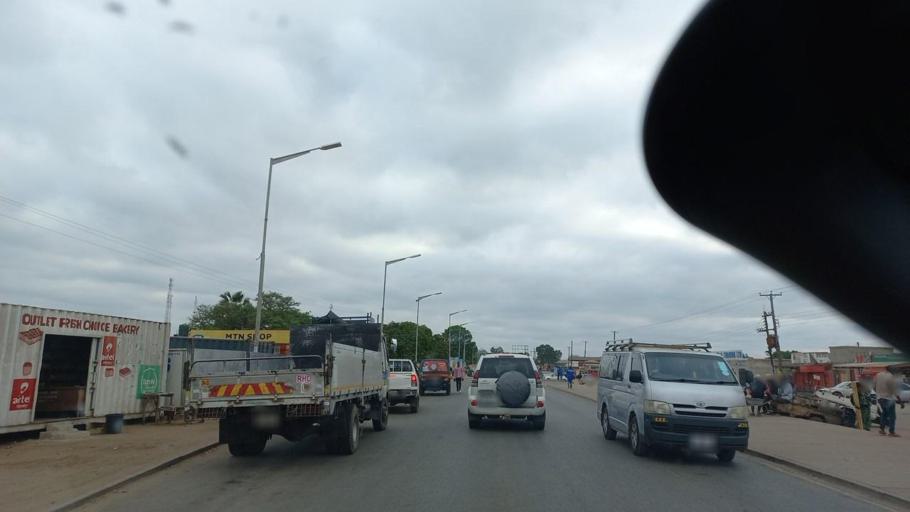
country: ZM
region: Lusaka
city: Chongwe
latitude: -15.3306
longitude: 28.6757
